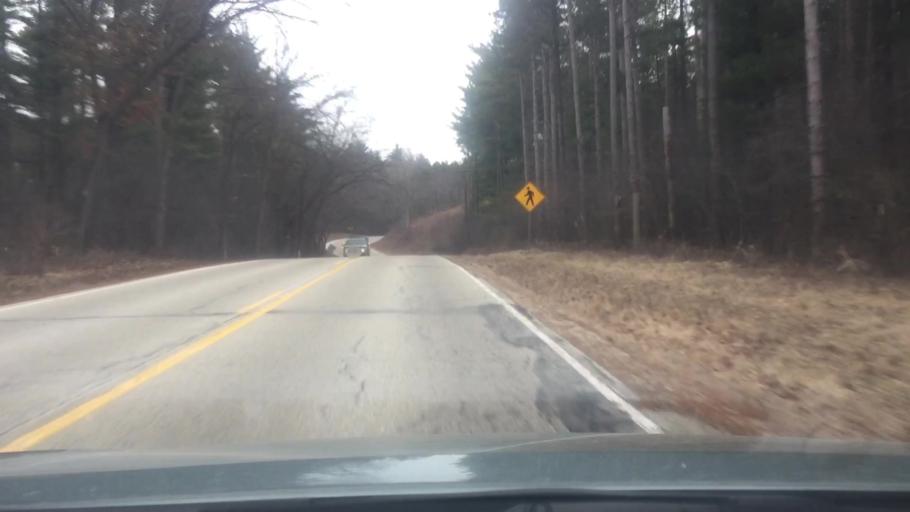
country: US
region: Wisconsin
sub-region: Waukesha County
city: North Prairie
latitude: 42.9410
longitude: -88.4595
